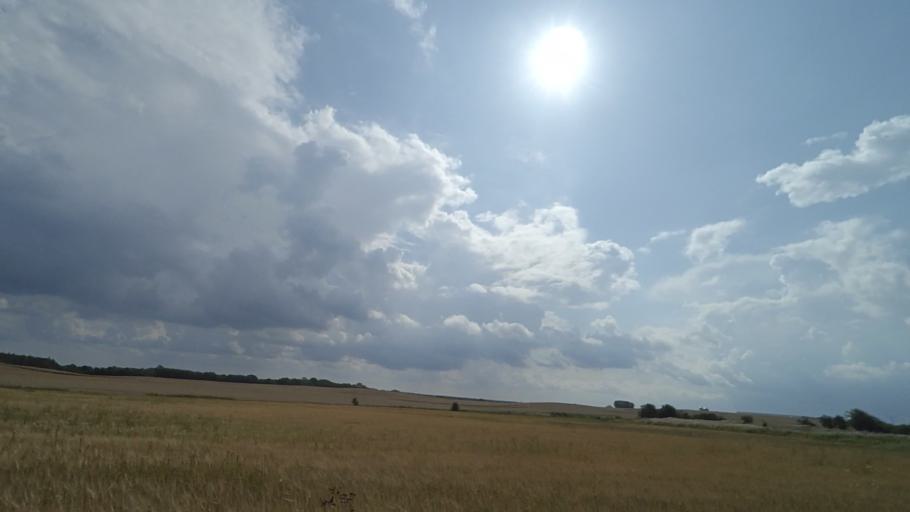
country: DK
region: Central Jutland
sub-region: Norddjurs Kommune
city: Allingabro
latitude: 56.5353
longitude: 10.3624
